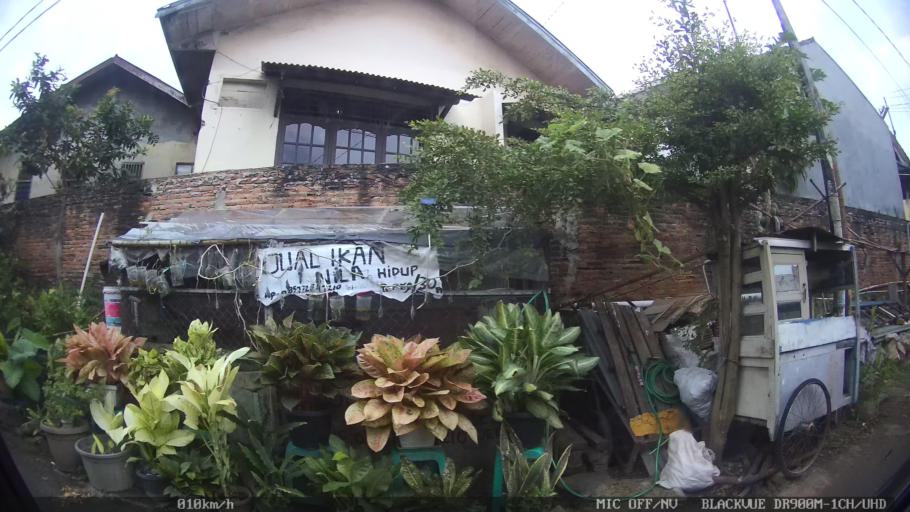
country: ID
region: Lampung
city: Bandarlampung
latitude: -5.4368
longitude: 105.2884
